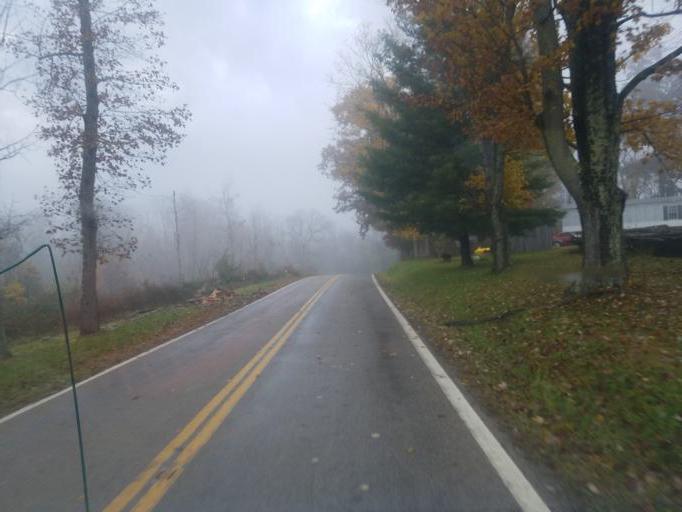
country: US
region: Ohio
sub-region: Morgan County
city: McConnelsville
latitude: 39.5011
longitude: -81.8974
